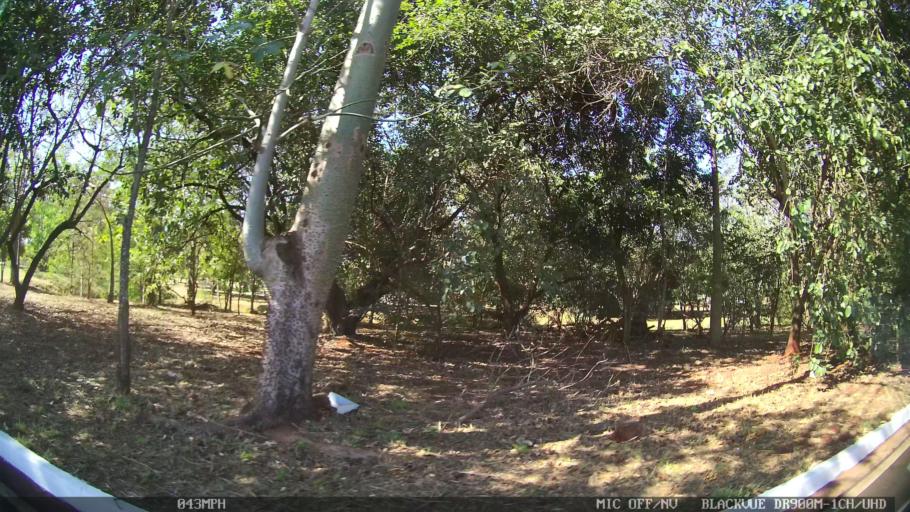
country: BR
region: Sao Paulo
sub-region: Ribeirao Preto
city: Ribeirao Preto
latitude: -21.2261
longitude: -47.7681
